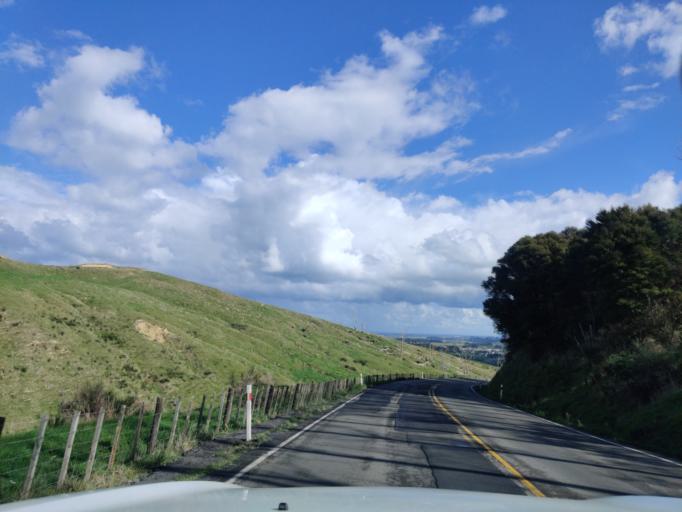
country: NZ
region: Manawatu-Wanganui
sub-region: Palmerston North City
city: Palmerston North
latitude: -40.2855
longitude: 175.7797
